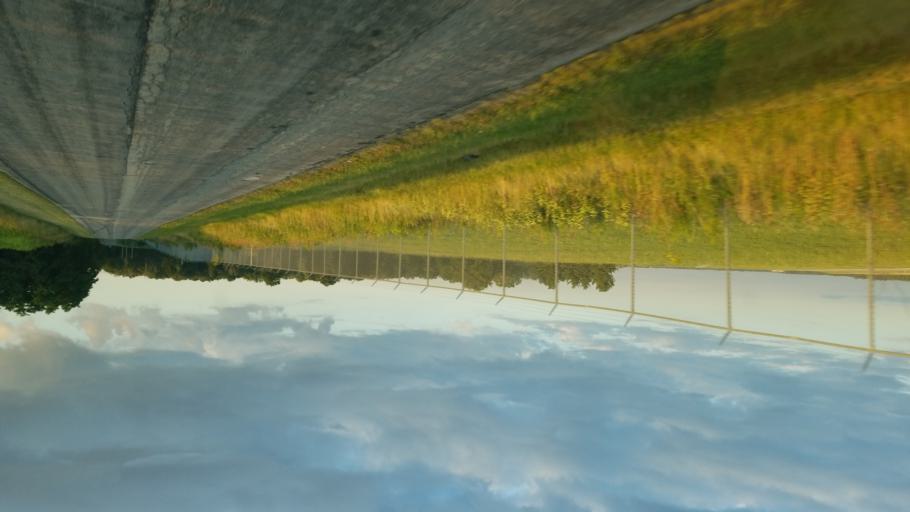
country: US
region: Ohio
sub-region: Richland County
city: Mansfield
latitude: 40.8340
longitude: -82.5328
